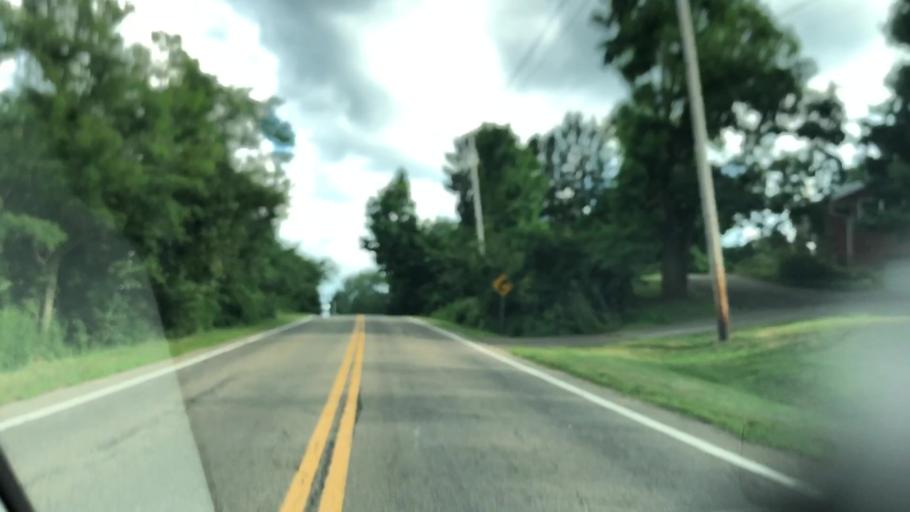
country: US
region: Ohio
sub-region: Summit County
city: Norton
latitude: 41.0639
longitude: -81.6382
